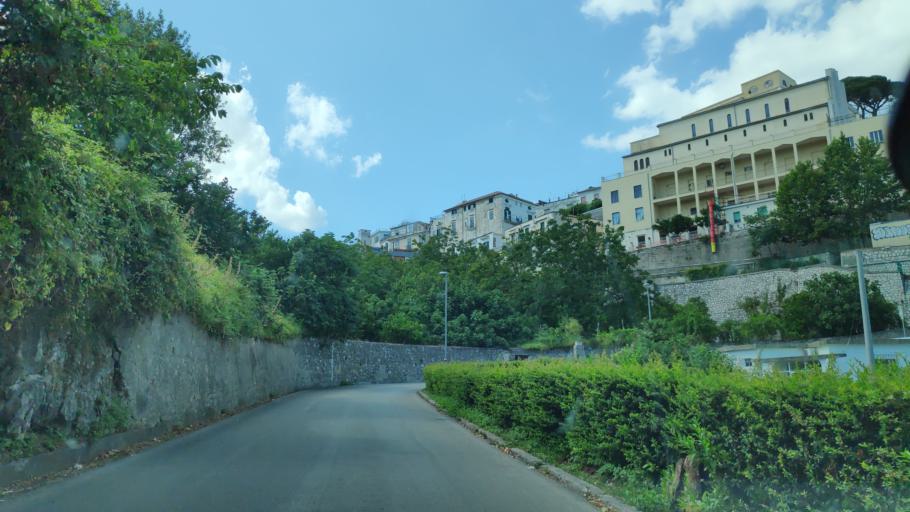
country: IT
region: Campania
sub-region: Provincia di Salerno
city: Vietri sul Mare
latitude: 40.6699
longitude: 14.7310
